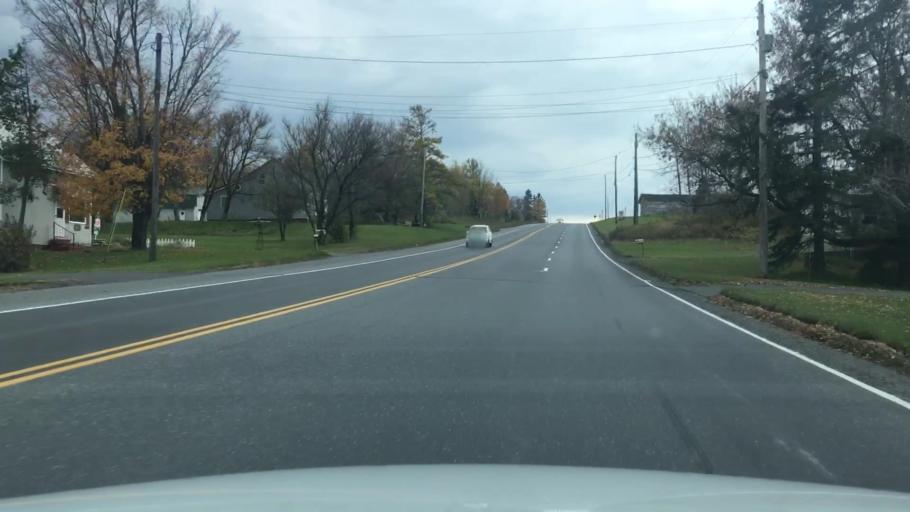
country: US
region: Maine
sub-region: Aroostook County
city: Caribou
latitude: 46.7829
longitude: -67.9890
